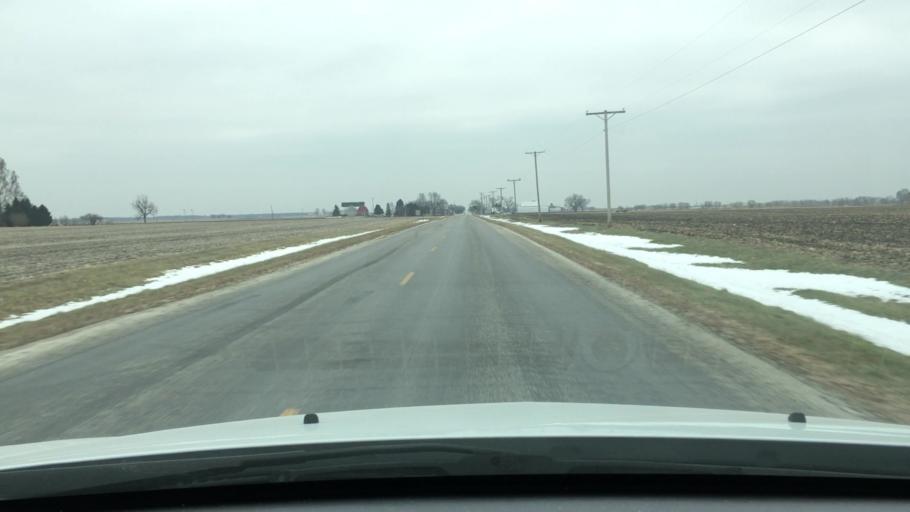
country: US
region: Illinois
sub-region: DeKalb County
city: Waterman
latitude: 41.7734
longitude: -88.7153
